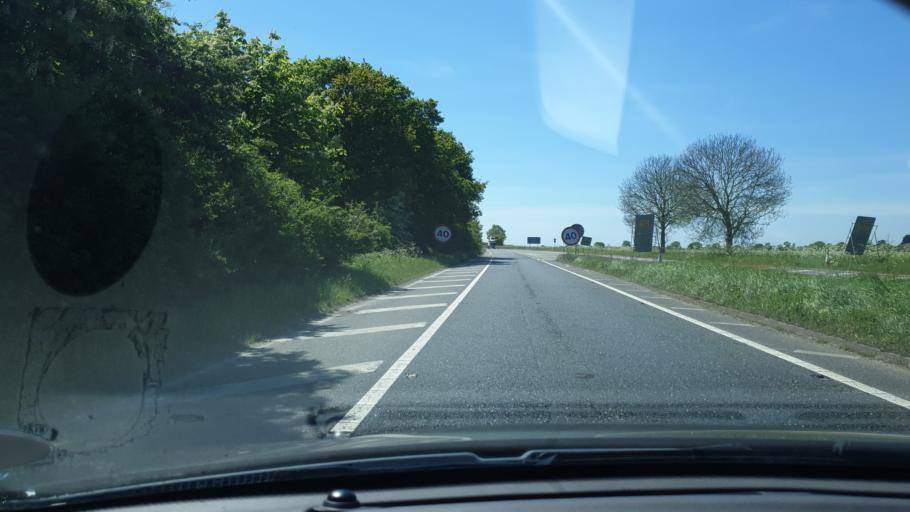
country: GB
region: England
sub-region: Essex
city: Great Bentley
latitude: 51.8958
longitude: 1.0682
